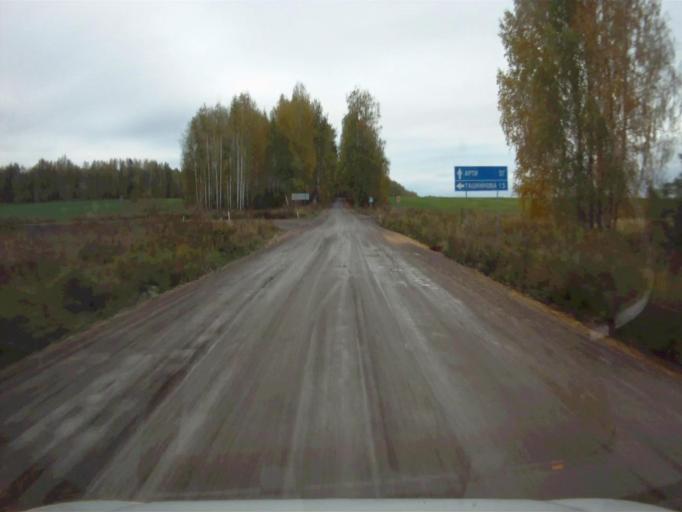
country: RU
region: Sverdlovsk
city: Mikhaylovsk
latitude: 56.1690
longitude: 59.2275
